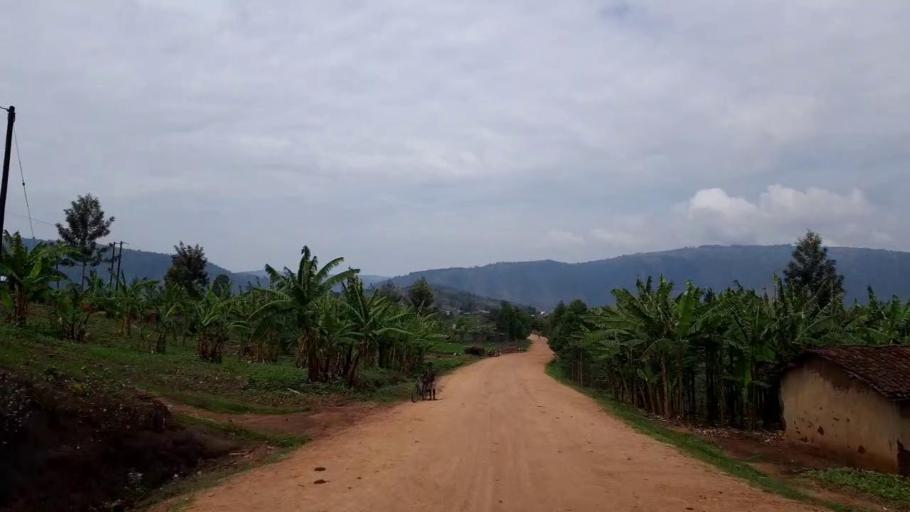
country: RW
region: Northern Province
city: Byumba
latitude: -1.4983
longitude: 30.2215
